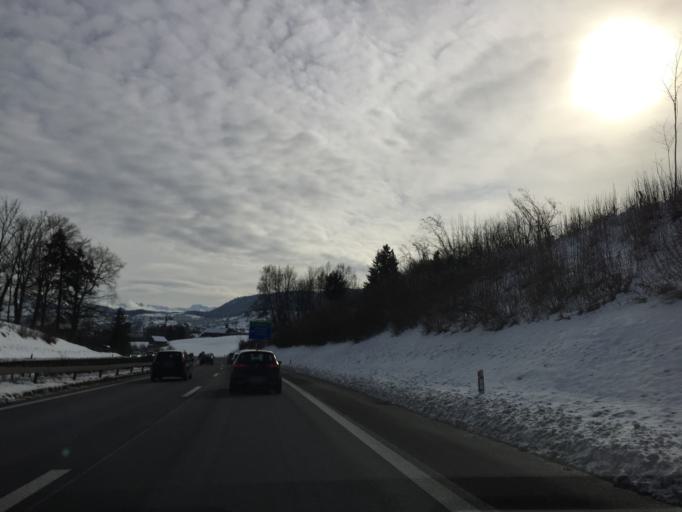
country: CH
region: Zurich
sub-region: Bezirk Horgen
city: Waedenswil / Eichweid
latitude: 47.2078
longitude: 8.6757
